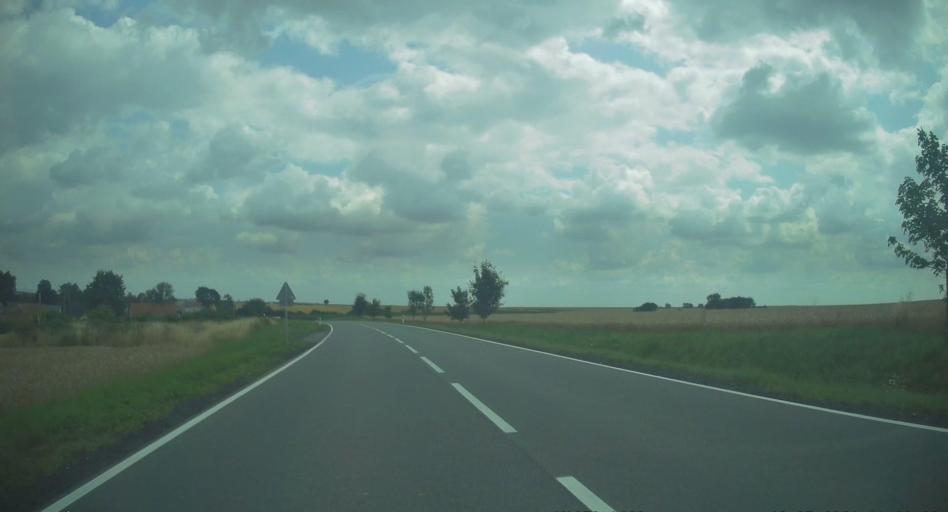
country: PL
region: Opole Voivodeship
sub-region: Powiat prudnicki
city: Raclawice Slaskie
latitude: 50.3494
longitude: 17.7768
